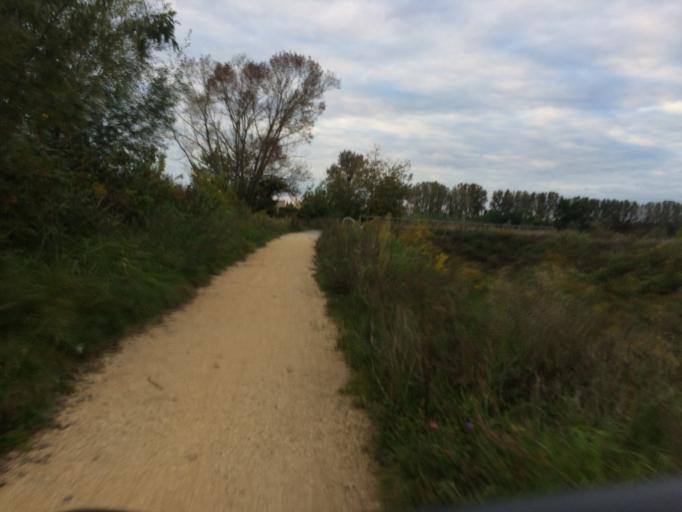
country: DE
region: Berlin
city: Heinersdorf
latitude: 52.5735
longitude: 13.4500
